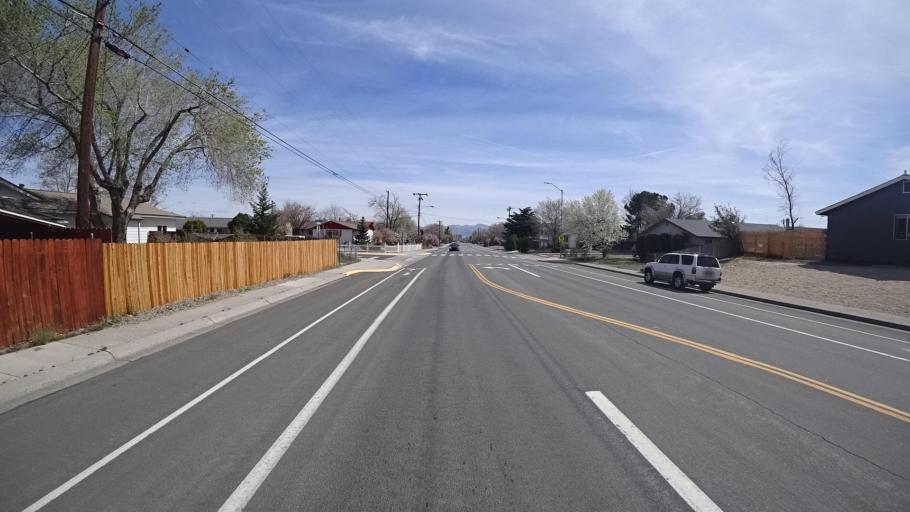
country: US
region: Nevada
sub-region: Washoe County
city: Reno
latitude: 39.5307
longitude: -119.8545
